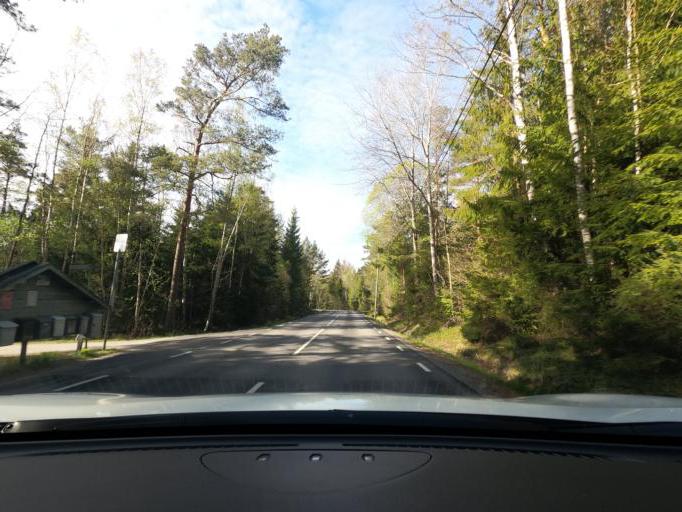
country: SE
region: Vaestra Goetaland
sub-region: Harryda Kommun
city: Landvetter
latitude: 57.6645
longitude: 12.2474
